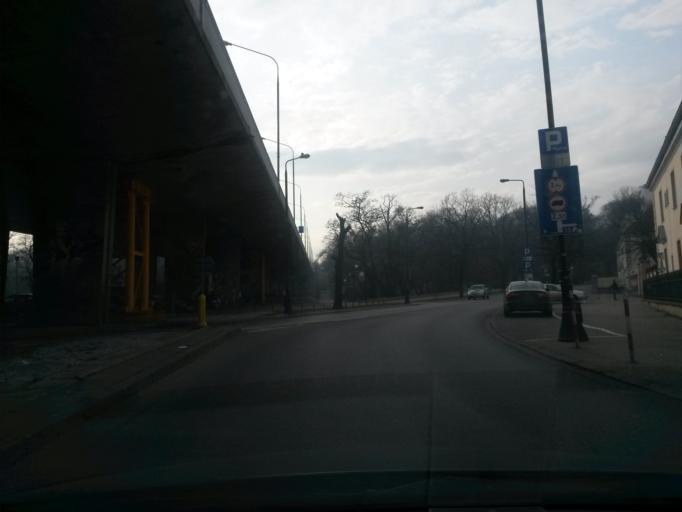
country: PL
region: Masovian Voivodeship
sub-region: Warszawa
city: Srodmiescie
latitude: 52.2222
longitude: 21.0354
